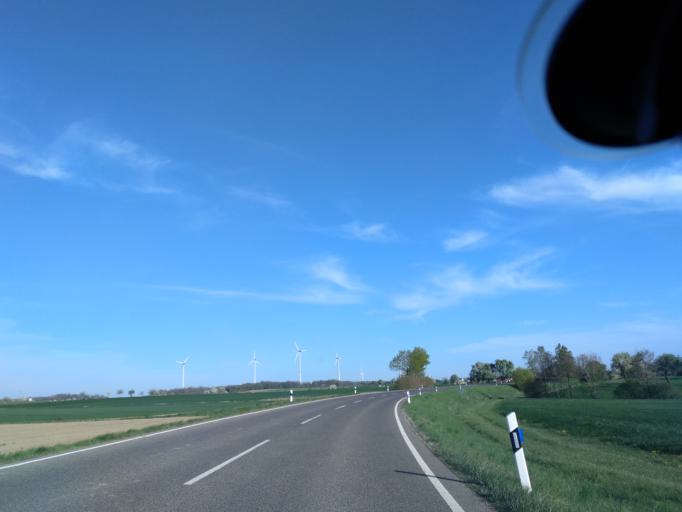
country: DE
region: Baden-Wuerttemberg
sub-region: Regierungsbezirk Stuttgart
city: Langenburg
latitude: 49.2109
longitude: 9.8632
